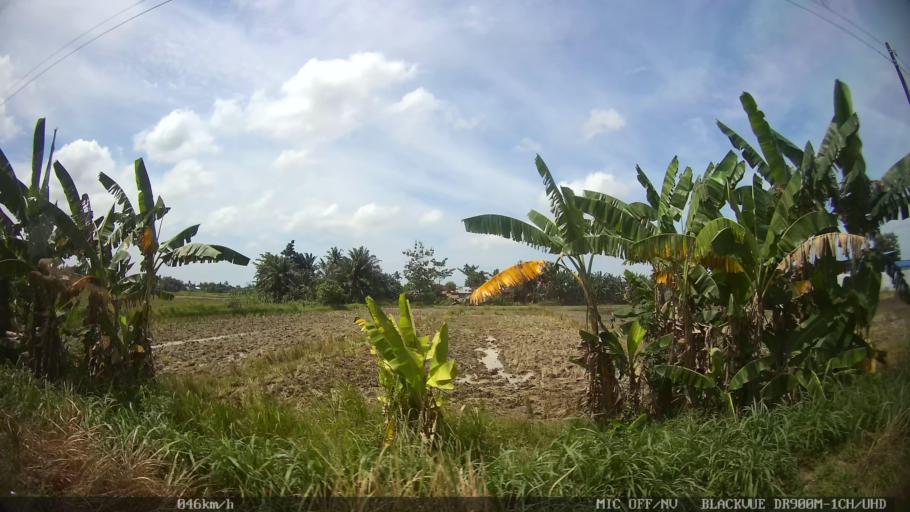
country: ID
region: North Sumatra
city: Percut
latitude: 3.5893
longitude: 98.8743
